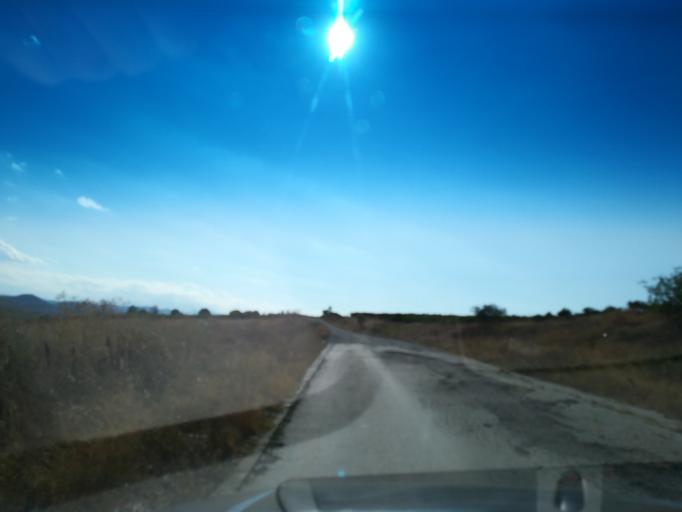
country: BG
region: Khaskovo
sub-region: Obshtina Mineralni Bani
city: Mineralni Bani
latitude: 41.9724
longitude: 25.3478
